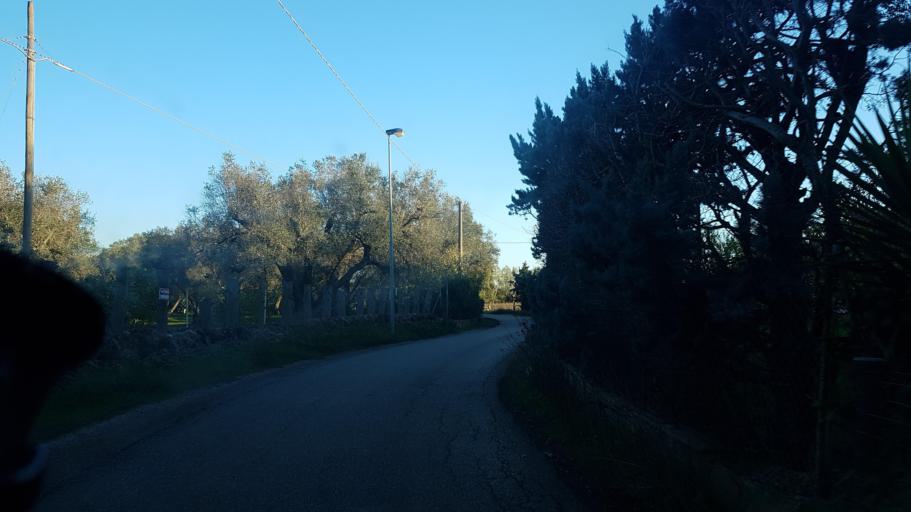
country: IT
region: Apulia
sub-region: Provincia di Brindisi
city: Mesagne
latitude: 40.5645
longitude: 17.7784
